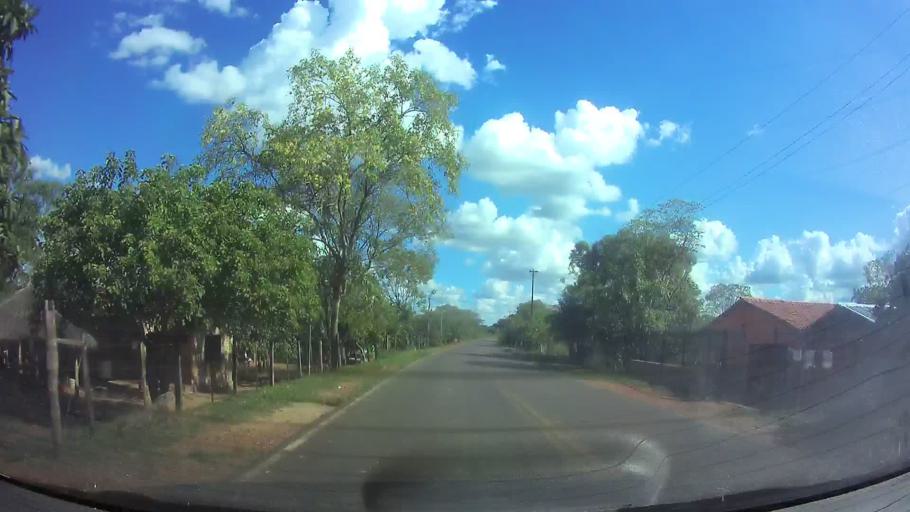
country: PY
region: Paraguari
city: Sapucai
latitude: -25.6737
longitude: -56.8618
